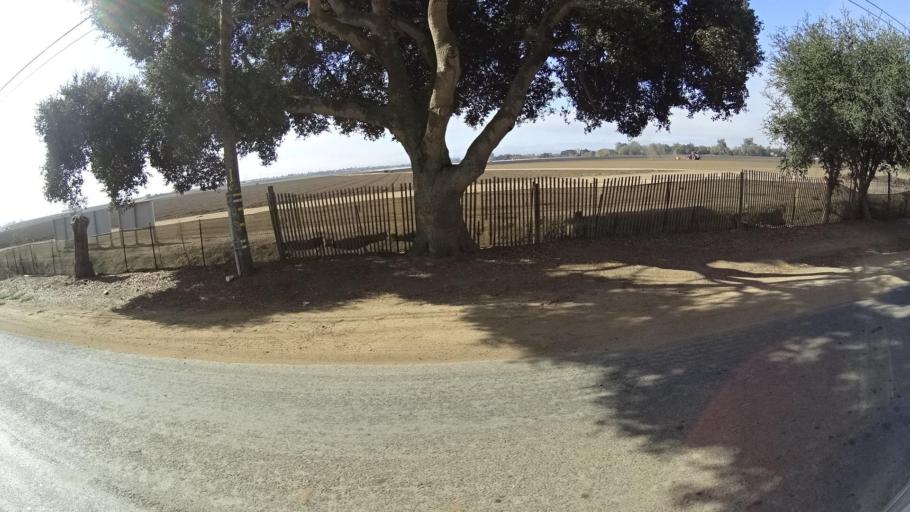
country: US
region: California
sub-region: Monterey County
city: Salinas
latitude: 36.7327
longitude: -121.6047
